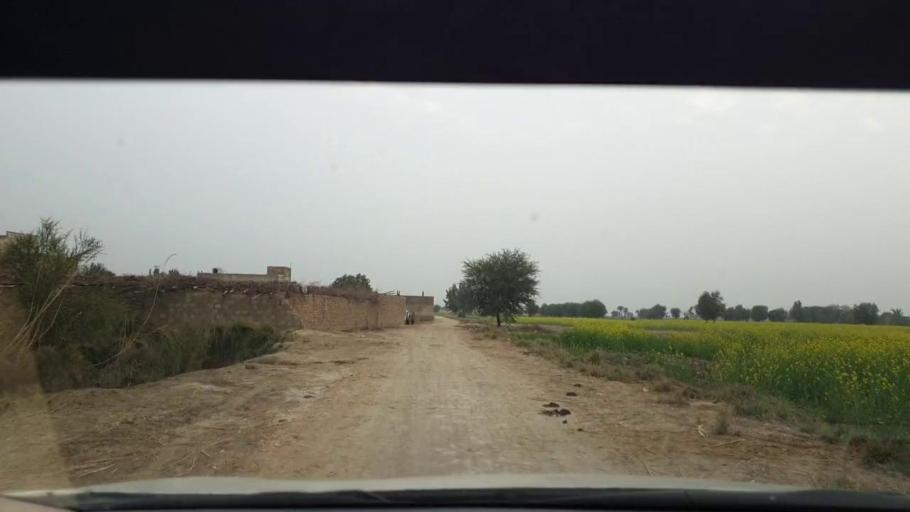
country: PK
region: Sindh
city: Jhol
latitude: 25.9237
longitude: 68.8544
